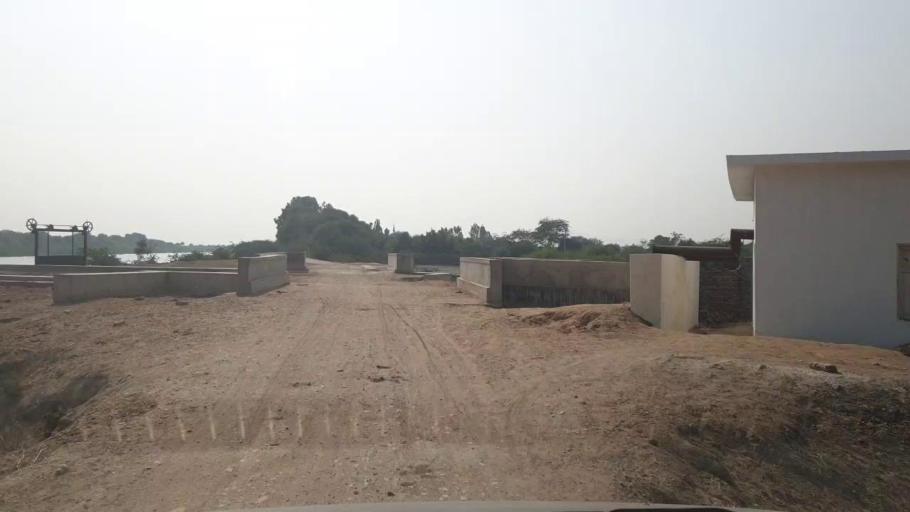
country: PK
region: Sindh
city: Tando Muhammad Khan
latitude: 25.0527
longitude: 68.3847
